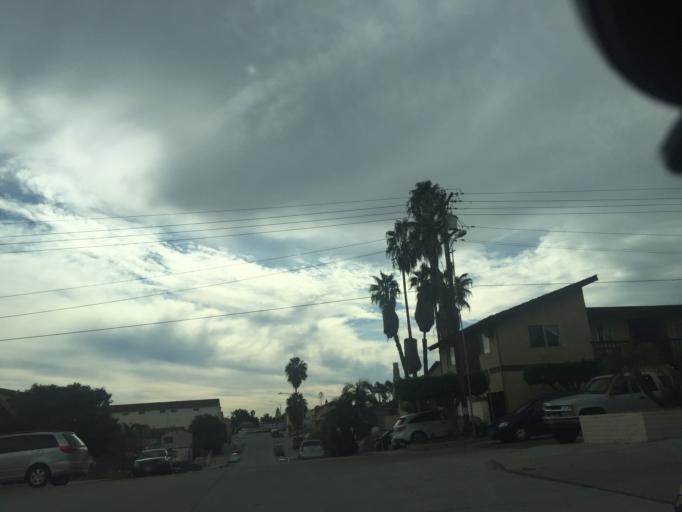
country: US
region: California
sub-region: San Diego County
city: Lemon Grove
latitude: 32.7516
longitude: -117.0912
